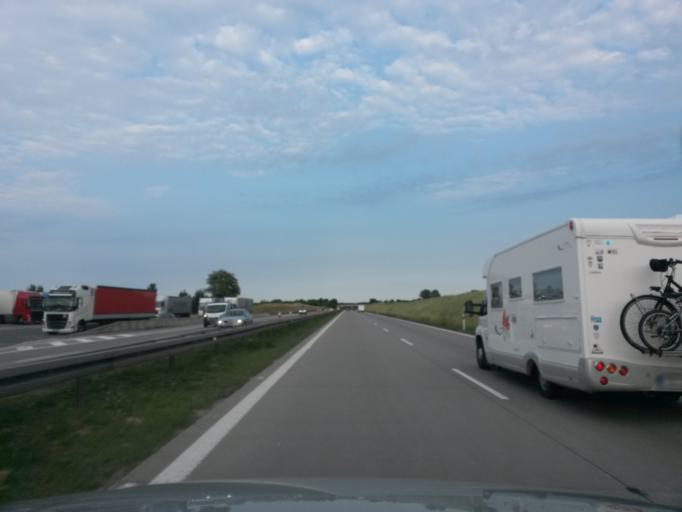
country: PL
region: Lower Silesian Voivodeship
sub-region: Powiat wroclawski
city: Katy Wroclawskie
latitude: 51.0303
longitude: 16.6482
